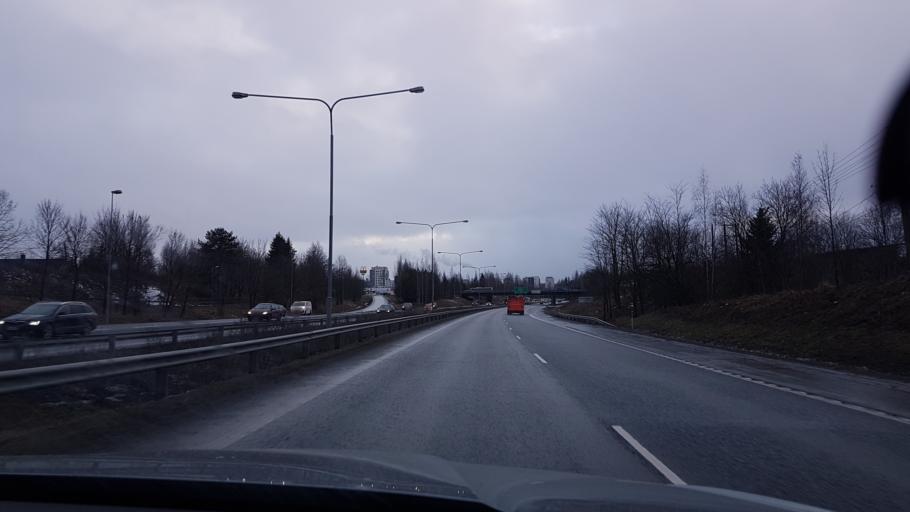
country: FI
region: Pirkanmaa
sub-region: Tampere
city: Tampere
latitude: 61.4815
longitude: 23.8725
